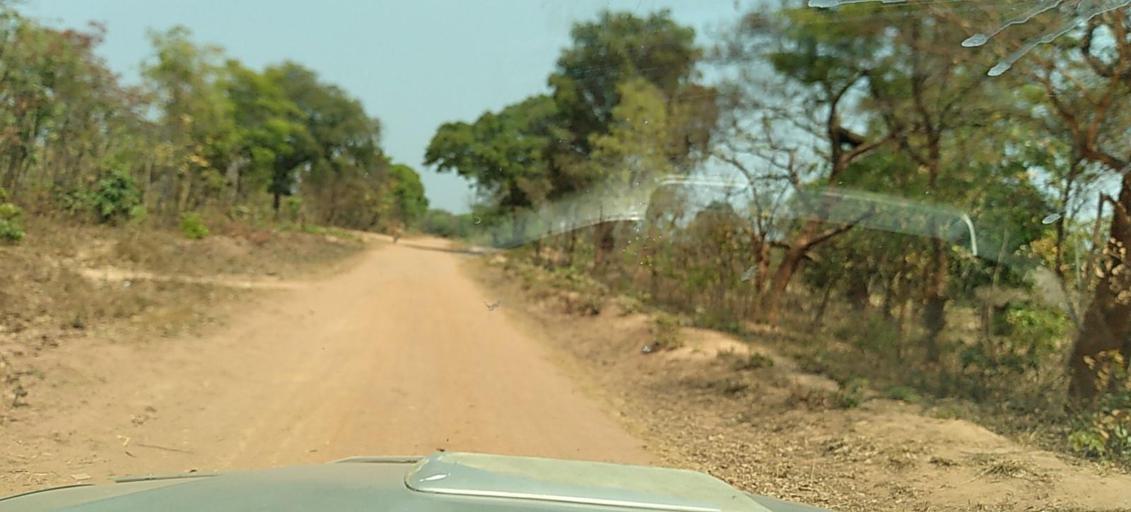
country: ZM
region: North-Western
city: Kasempa
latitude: -13.6940
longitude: 26.3255
